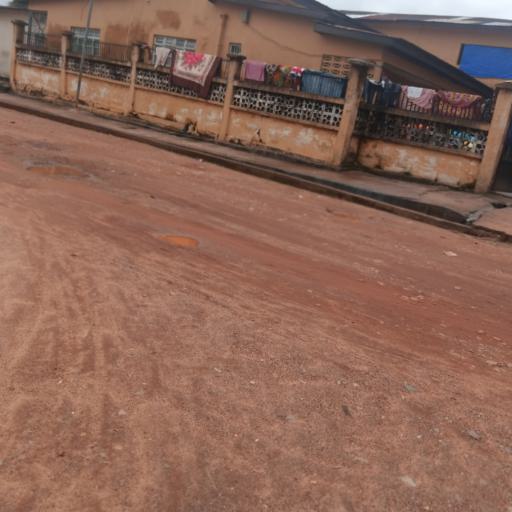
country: SL
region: Eastern Province
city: Kenema
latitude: 7.8868
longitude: -11.1875
